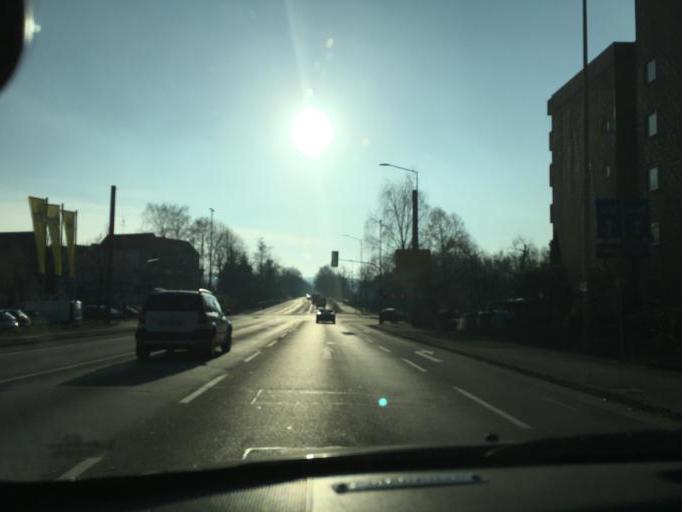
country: DE
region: North Rhine-Westphalia
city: Schwerte
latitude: 51.4436
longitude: 7.5725
